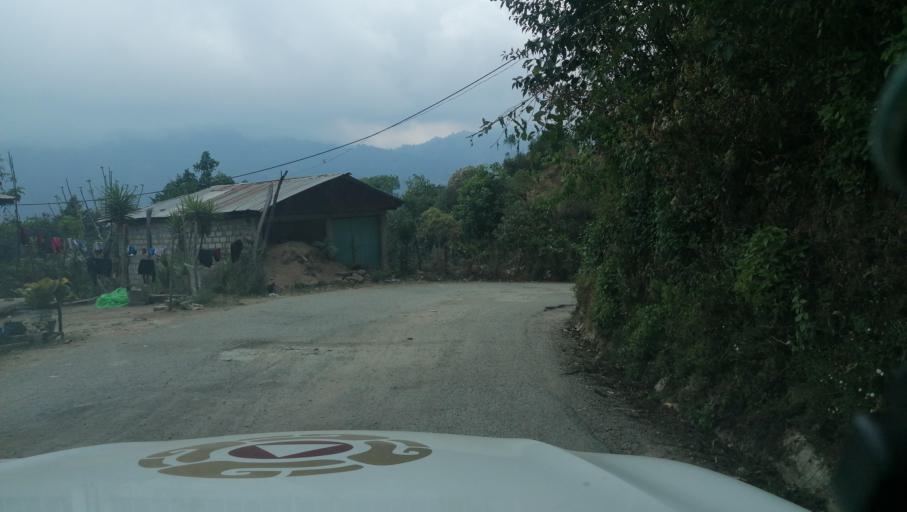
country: GT
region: San Marcos
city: Tacana
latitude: 15.2044
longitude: -92.1866
